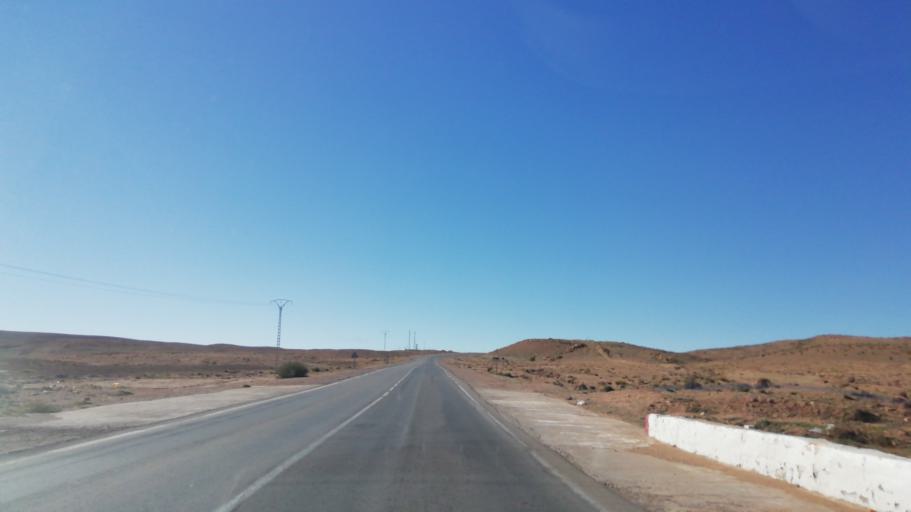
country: DZ
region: El Bayadh
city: El Bayadh
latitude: 33.6682
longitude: 1.4379
